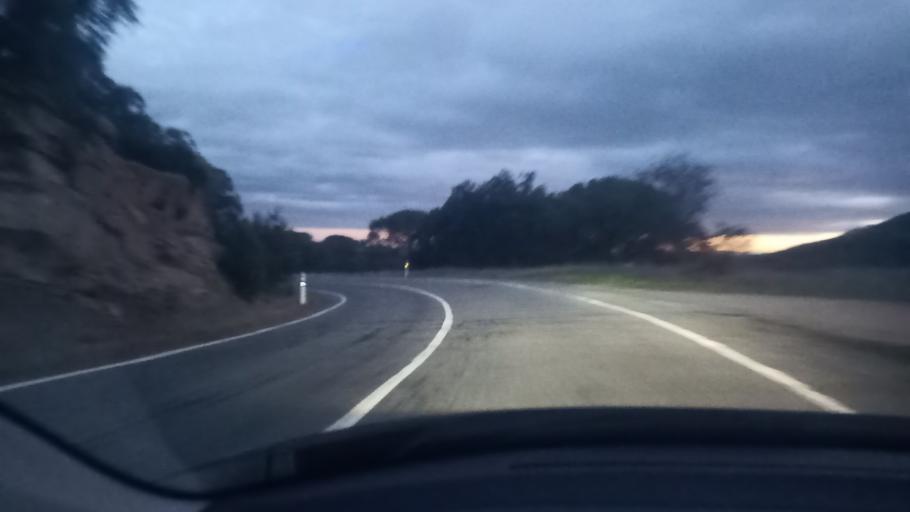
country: ES
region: Madrid
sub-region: Provincia de Madrid
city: Navas del Rey
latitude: 40.4321
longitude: -4.2604
